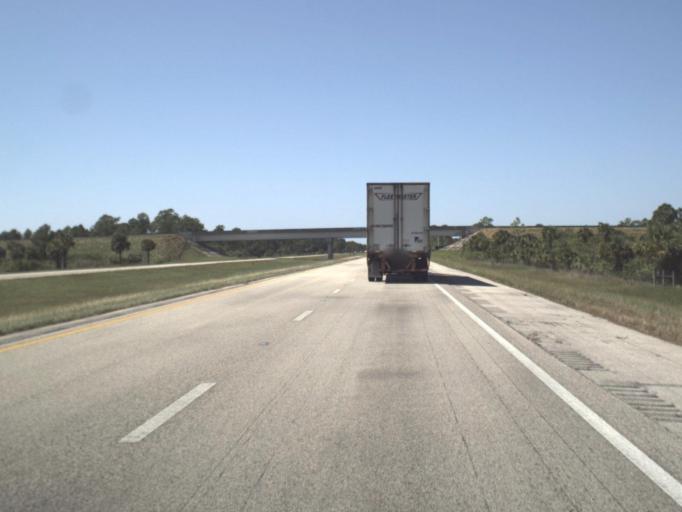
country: US
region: Florida
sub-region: Collier County
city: Orangetree
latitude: 26.1531
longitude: -81.5407
